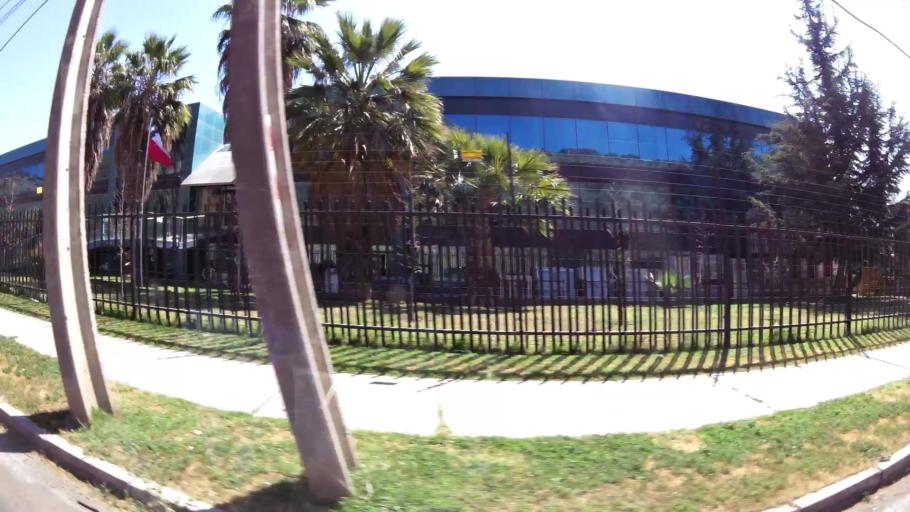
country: CL
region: Santiago Metropolitan
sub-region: Provincia de Santiago
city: Lo Prado
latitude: -33.3822
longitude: -70.7417
